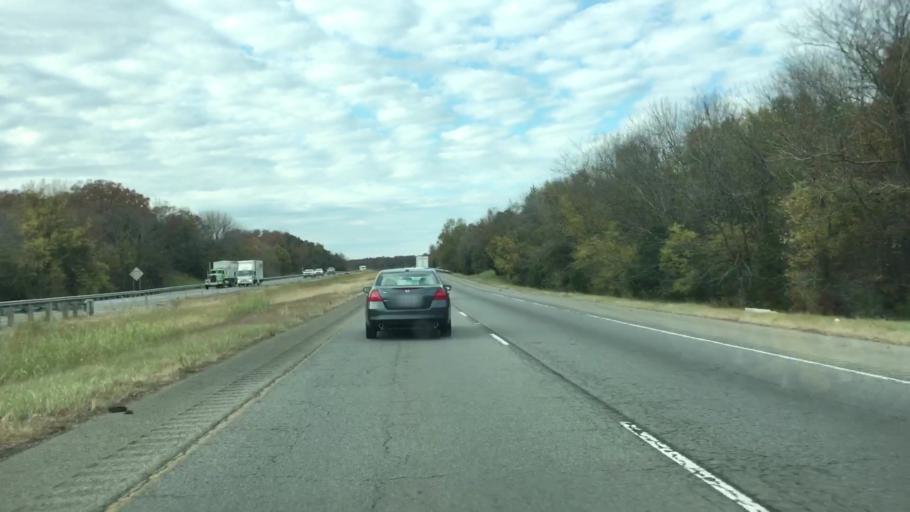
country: US
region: Arkansas
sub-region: Faulkner County
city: Conway
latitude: 35.1317
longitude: -92.5157
